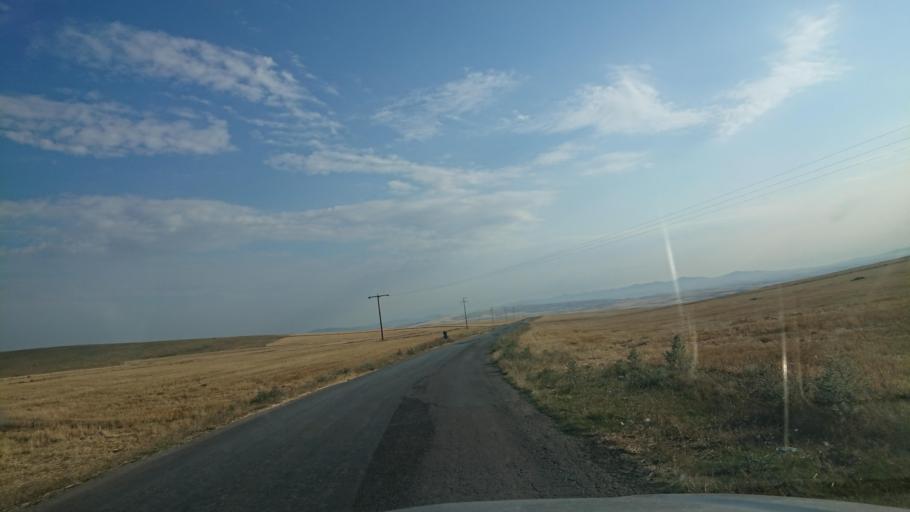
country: TR
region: Aksaray
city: Ortakoy
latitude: 38.7785
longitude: 34.0607
